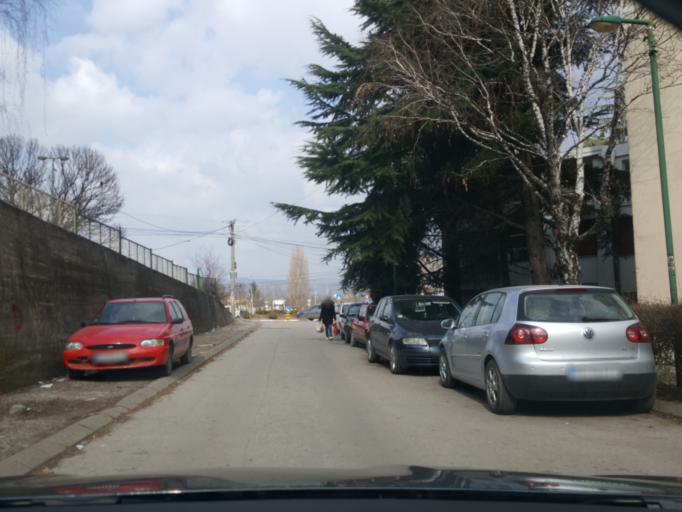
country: RS
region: Central Serbia
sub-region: Nisavski Okrug
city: Nis
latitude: 43.3141
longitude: 21.8642
